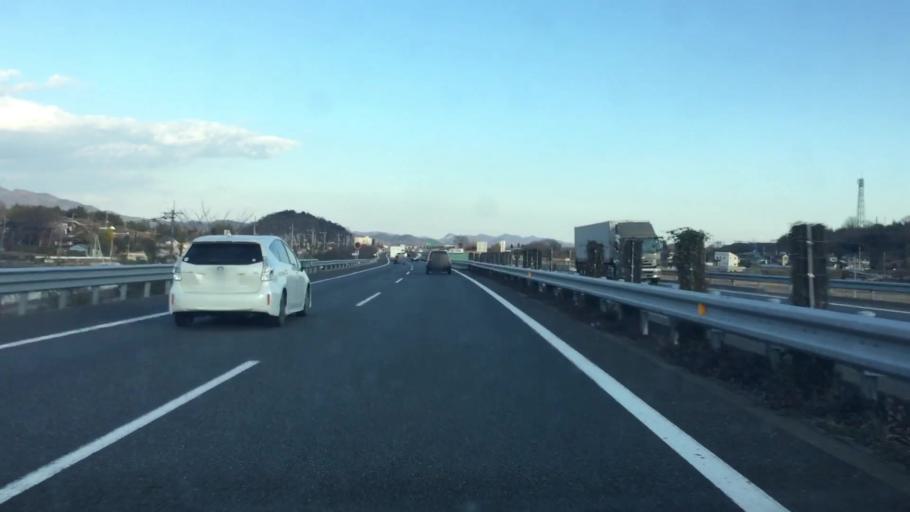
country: JP
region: Gunma
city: Ota
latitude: 36.3361
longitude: 139.3590
